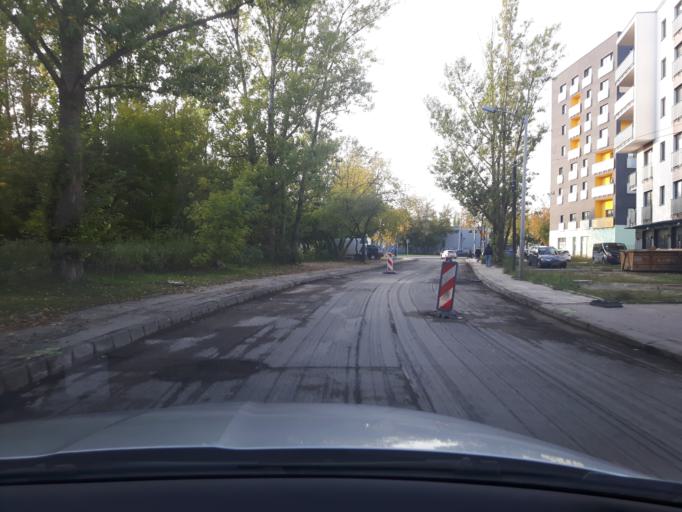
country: PL
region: Masovian Voivodeship
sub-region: Warszawa
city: Wlochy
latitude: 52.1659
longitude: 20.9935
